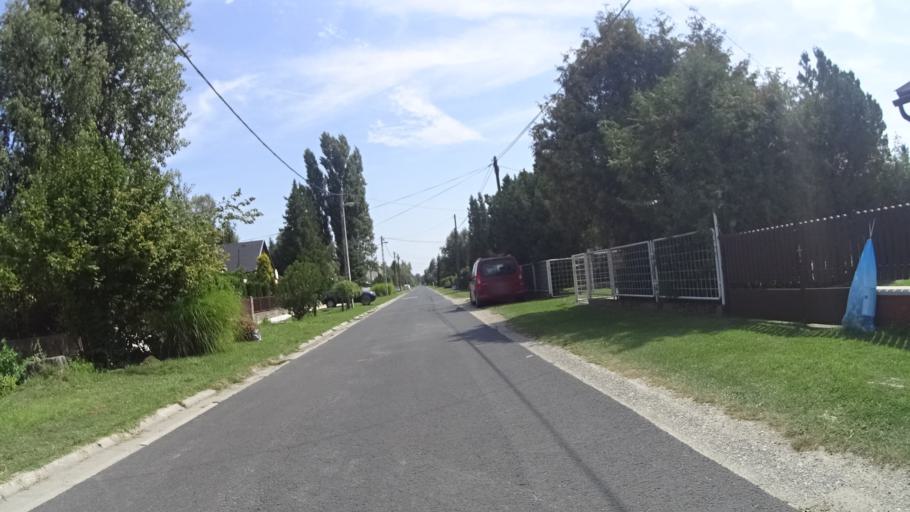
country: HU
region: Somogy
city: Kethely
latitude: 46.7033
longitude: 17.3994
